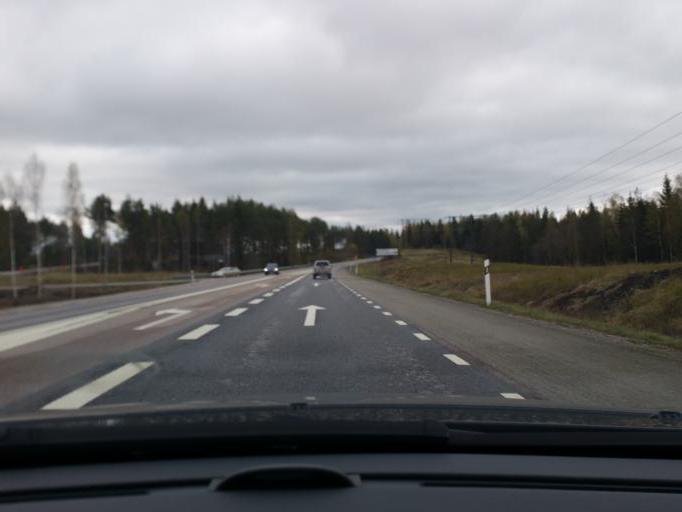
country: SE
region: Kronoberg
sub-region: Vaxjo Kommun
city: Vaexjoe
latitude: 56.8628
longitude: 14.8478
